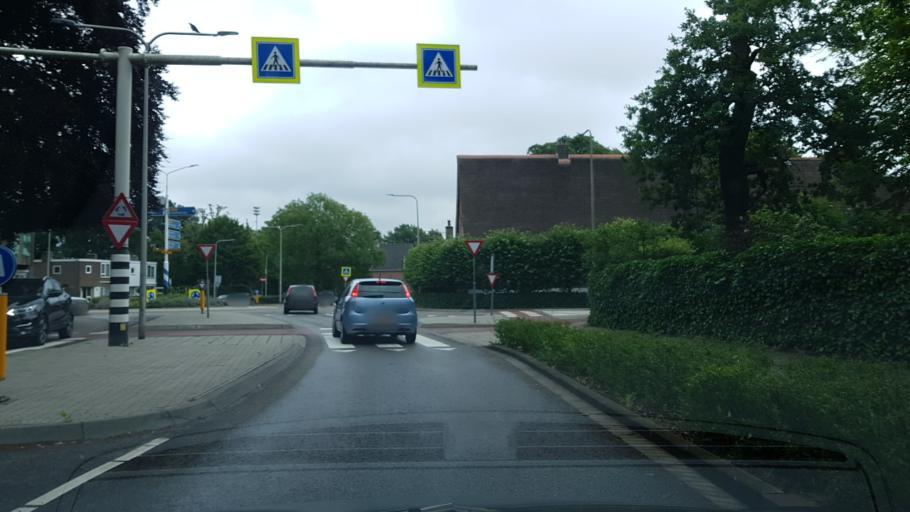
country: NL
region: North Holland
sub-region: Gemeente Heemstede
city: Heemstede
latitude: 52.3611
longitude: 4.5980
